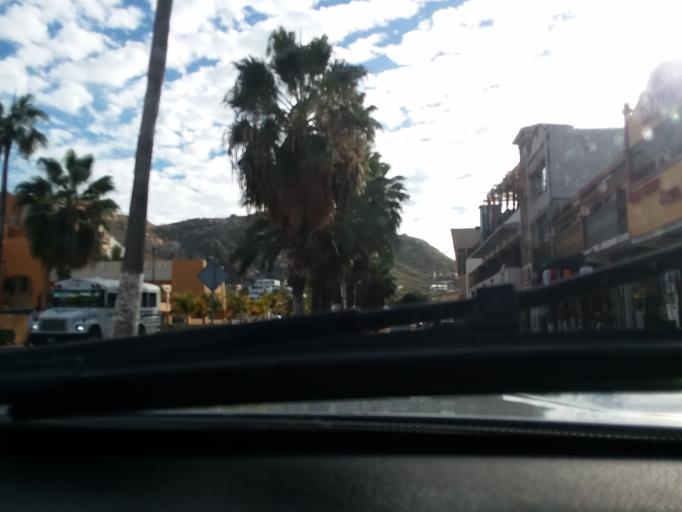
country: MX
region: Baja California Sur
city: Cabo San Lucas
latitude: 22.8818
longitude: -109.9123
